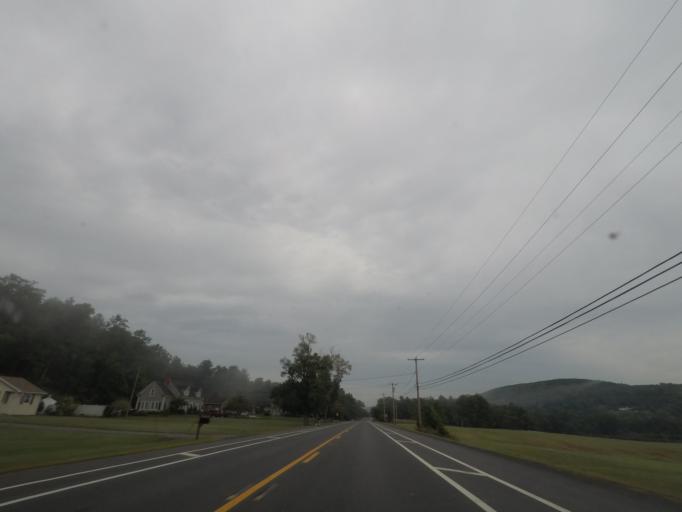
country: US
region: Massachusetts
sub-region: Hampden County
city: Palmer
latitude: 42.1494
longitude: -72.2726
